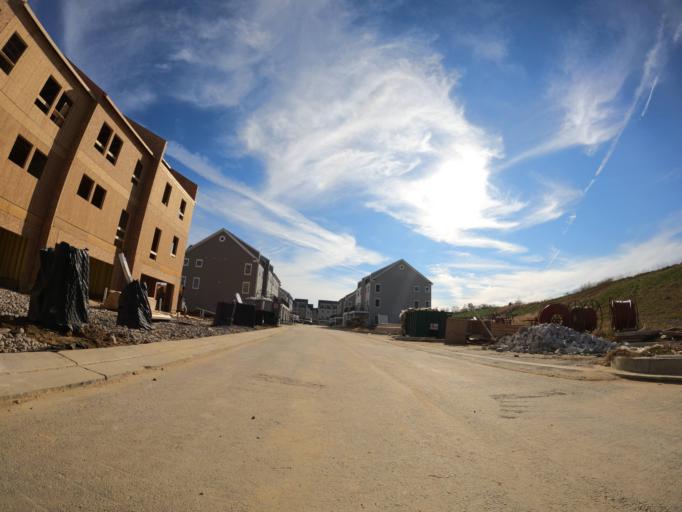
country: US
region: Maryland
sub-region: Carroll County
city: Sykesville
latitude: 39.3795
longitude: -76.9652
